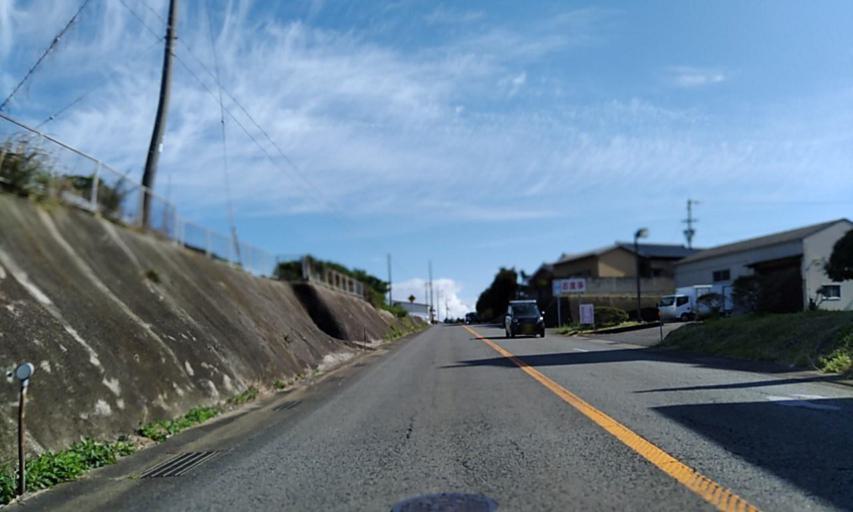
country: JP
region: Wakayama
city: Gobo
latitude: 33.8268
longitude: 135.1872
